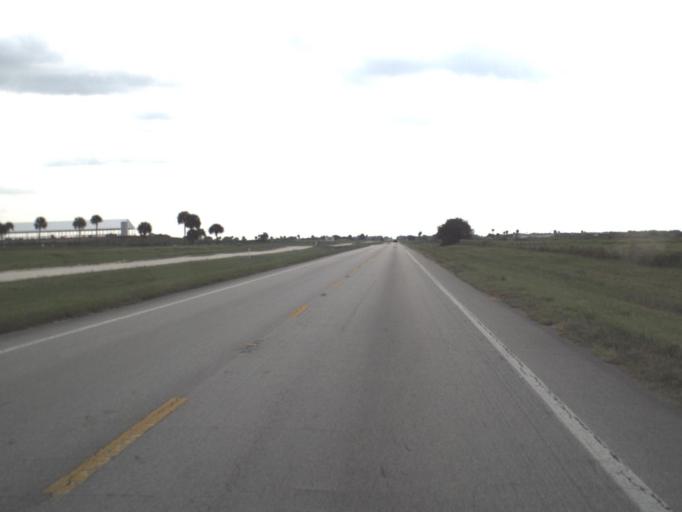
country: US
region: Florida
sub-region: Okeechobee County
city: Cypress Quarters
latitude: 27.4276
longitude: -80.8124
